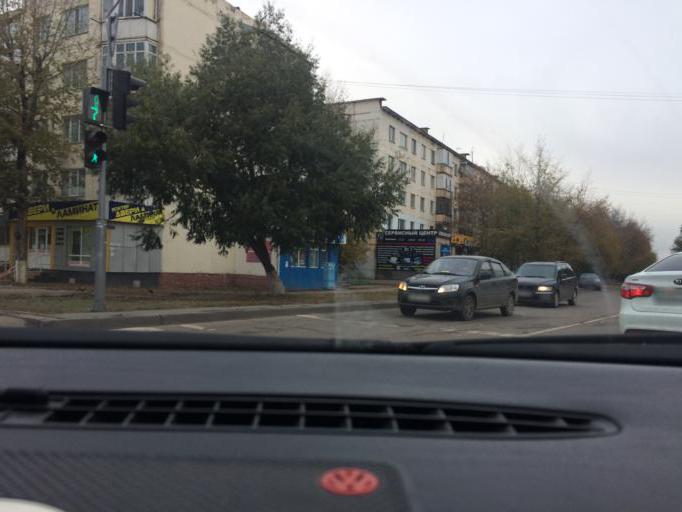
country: KZ
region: Astana Qalasy
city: Astana
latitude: 51.1462
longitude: 71.4658
